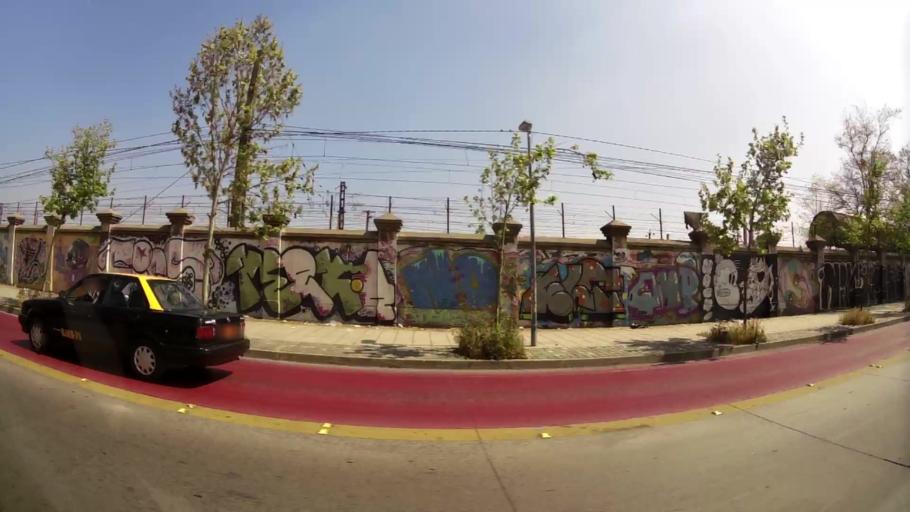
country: CL
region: Santiago Metropolitan
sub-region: Provincia de Santiago
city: Santiago
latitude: -33.4572
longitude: -70.6783
